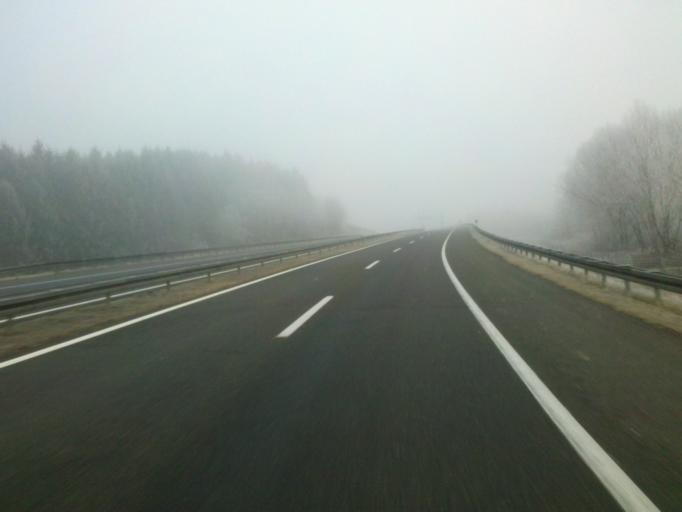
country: HR
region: Varazdinska
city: Jalzabet
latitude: 46.2465
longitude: 16.4006
